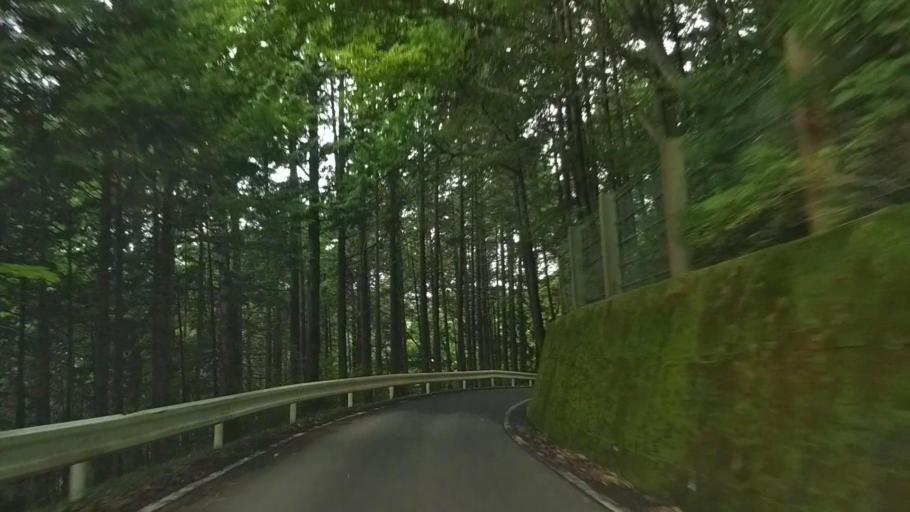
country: JP
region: Shizuoka
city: Gotemba
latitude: 35.3276
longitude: 138.9845
